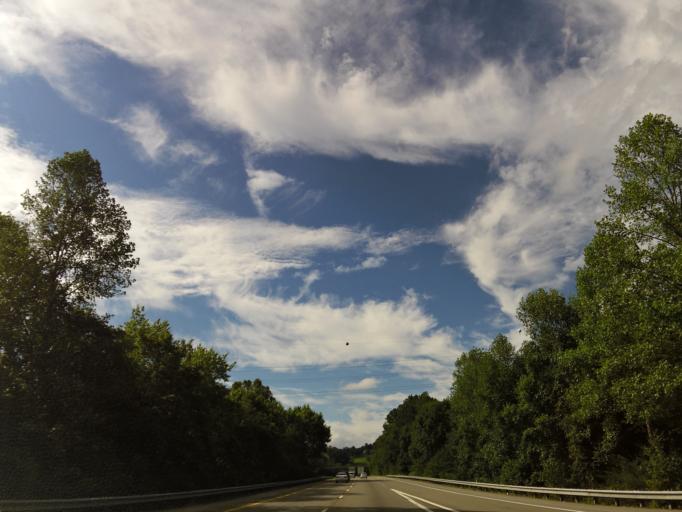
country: US
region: Tennessee
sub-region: Loudon County
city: Lenoir City
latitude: 35.8661
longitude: -84.2587
